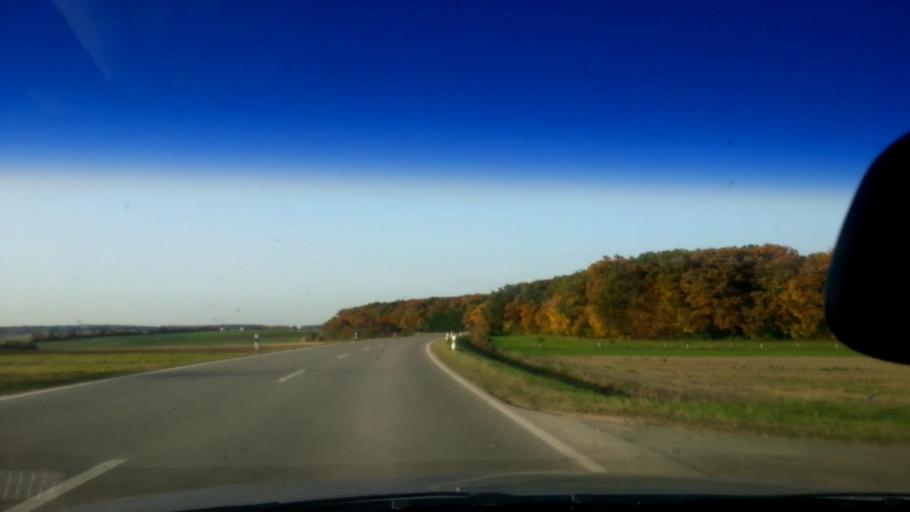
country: DE
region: Bavaria
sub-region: Upper Franconia
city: Schesslitz
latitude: 49.9877
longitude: 11.0276
